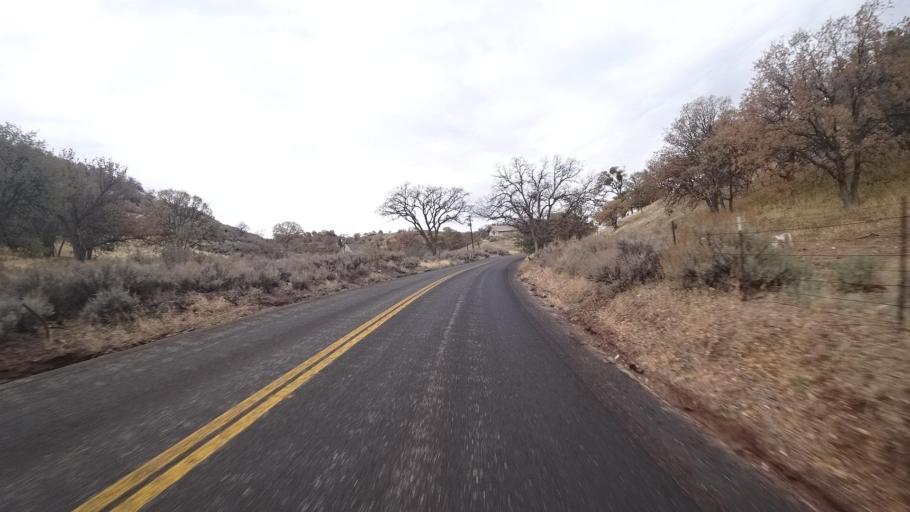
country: US
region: California
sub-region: Kern County
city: Golden Hills
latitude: 35.0940
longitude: -118.5461
